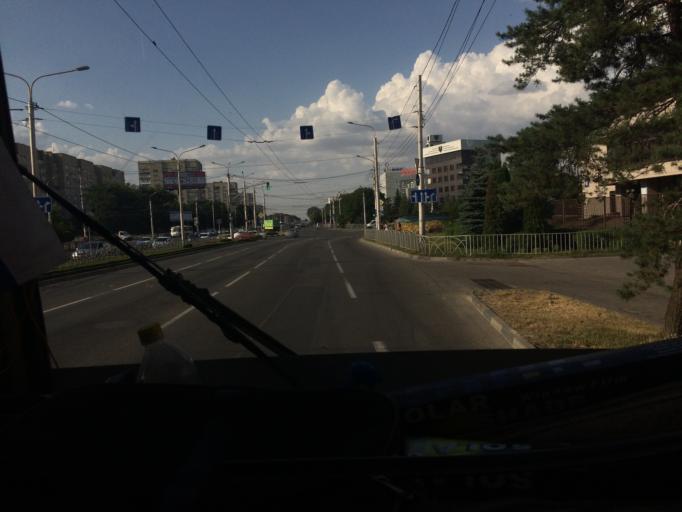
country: RU
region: Stavropol'skiy
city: Stavropol'
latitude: 45.0184
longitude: 41.9327
